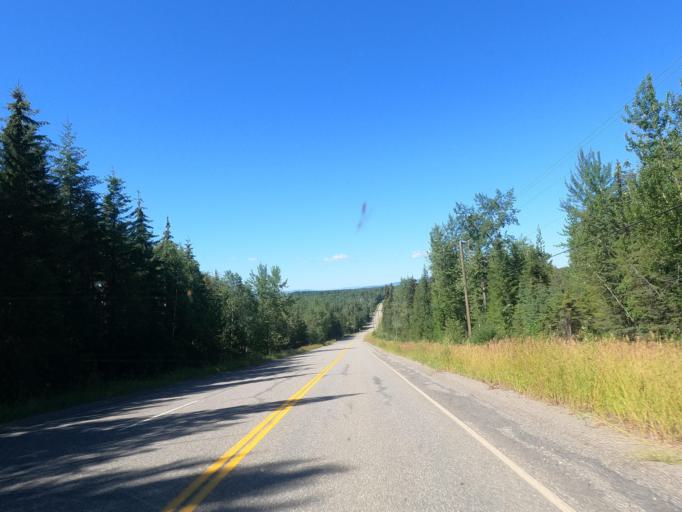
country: CA
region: British Columbia
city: Quesnel
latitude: 53.0236
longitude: -122.3563
